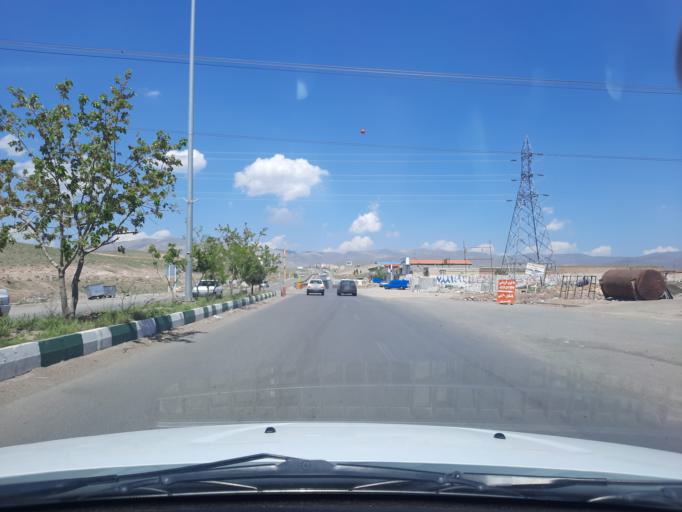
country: IR
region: Qazvin
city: Alvand
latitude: 36.2788
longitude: 50.1271
